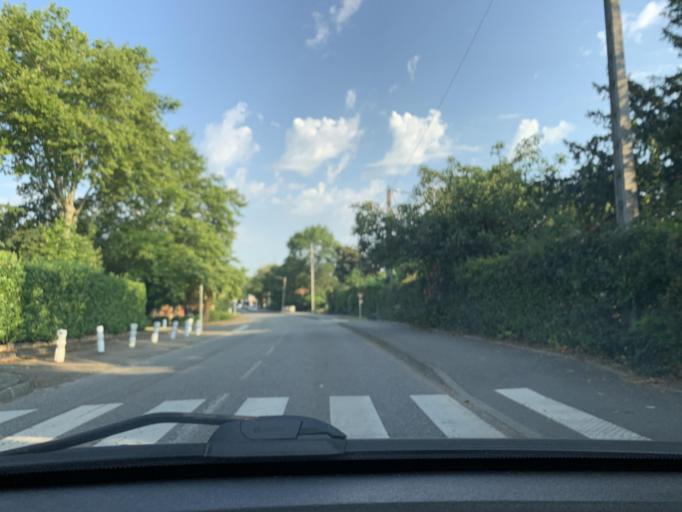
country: FR
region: Midi-Pyrenees
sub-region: Departement de la Haute-Garonne
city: Labege
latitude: 43.5336
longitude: 1.5325
